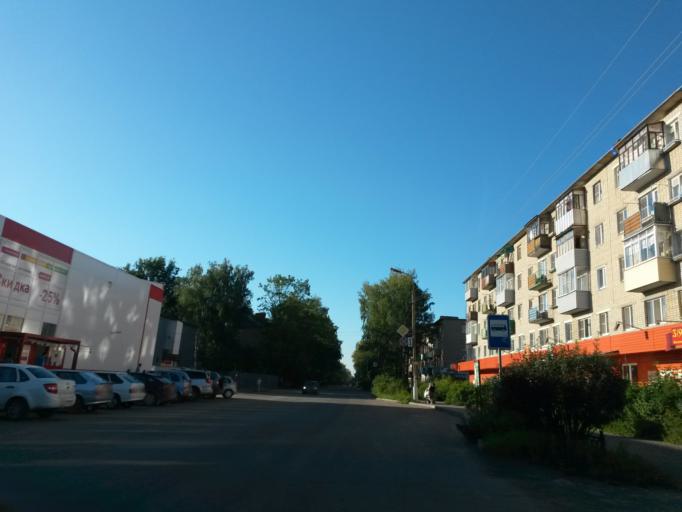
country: RU
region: Jaroslavl
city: Gavrilov-Yam
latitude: 57.2998
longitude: 39.8644
